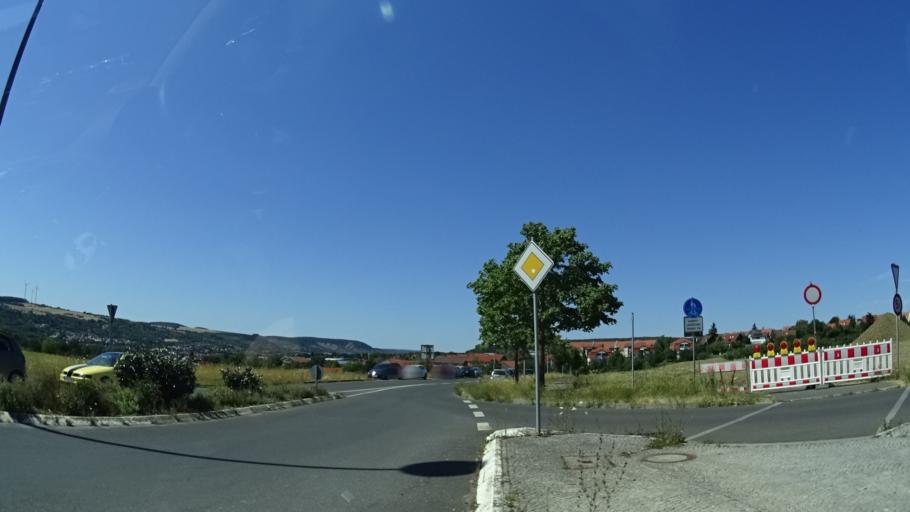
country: DE
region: Bavaria
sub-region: Regierungsbezirk Unterfranken
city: Veitshochheim
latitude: 49.8277
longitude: 9.8907
